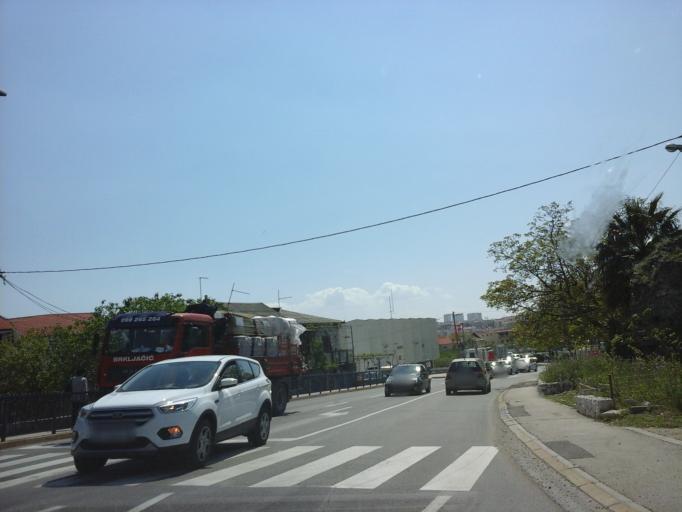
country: HR
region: Splitsko-Dalmatinska
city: Solin
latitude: 43.5419
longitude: 16.4914
